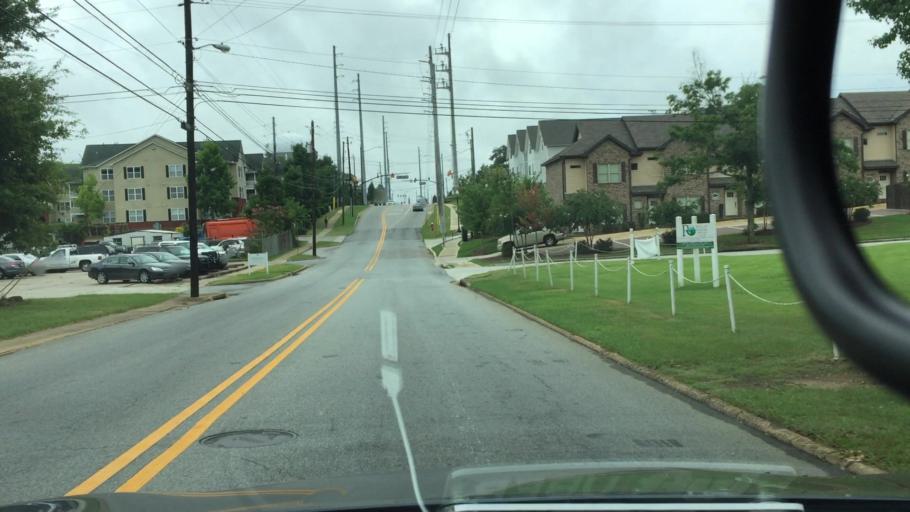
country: US
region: Alabama
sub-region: Lee County
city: Auburn
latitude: 32.6126
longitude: -85.4904
